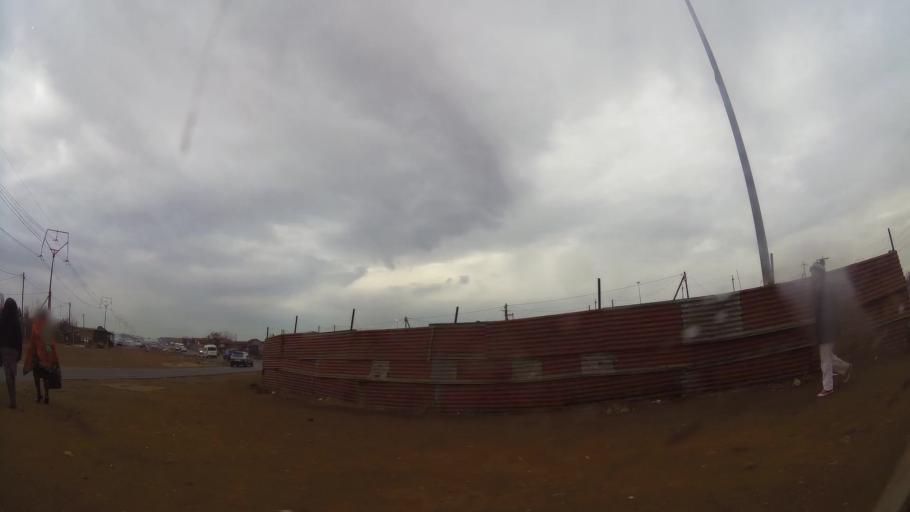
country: ZA
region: Gauteng
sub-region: Ekurhuleni Metropolitan Municipality
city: Germiston
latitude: -26.3711
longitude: 28.1693
